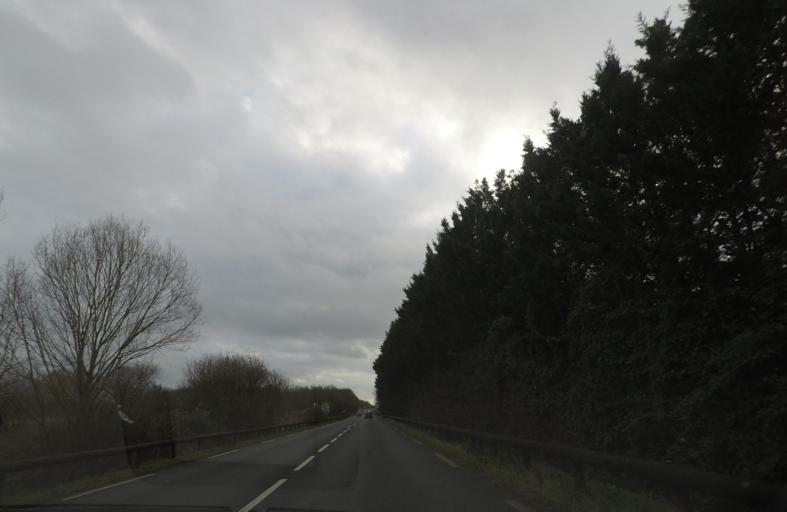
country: FR
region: Centre
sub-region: Departement du Loir-et-Cher
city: Soings-en-Sologne
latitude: 47.4587
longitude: 1.5236
